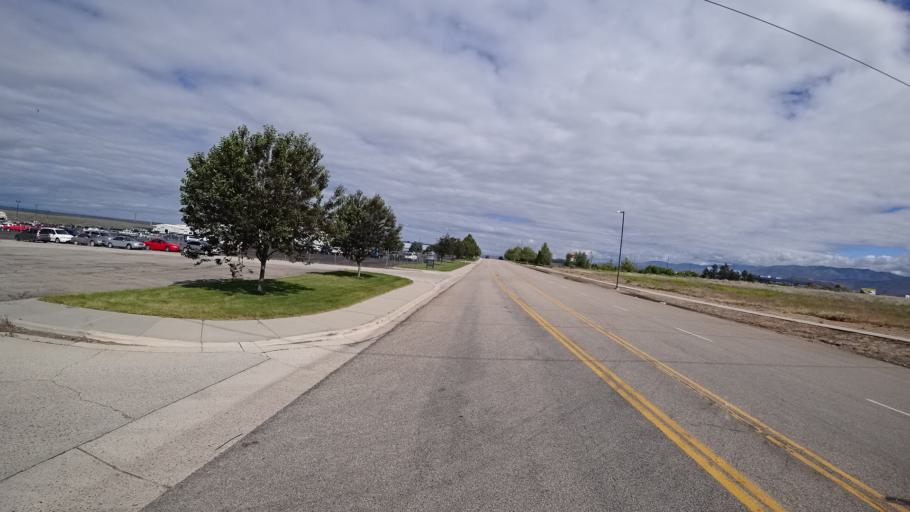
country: US
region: Idaho
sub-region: Ada County
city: Boise
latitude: 43.5346
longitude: -116.1604
